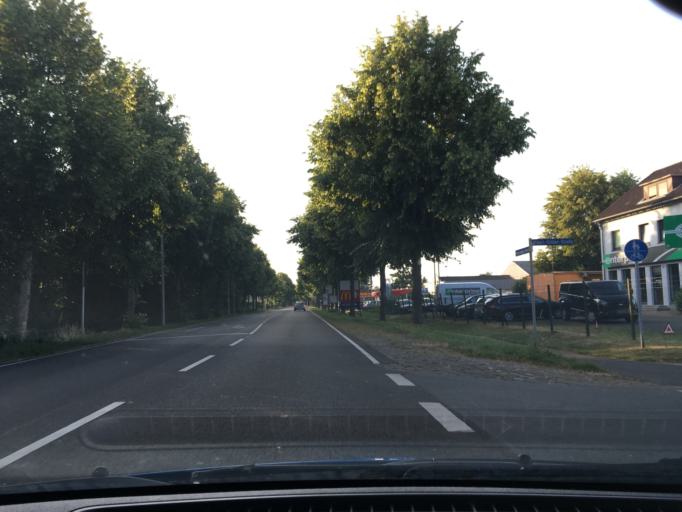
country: DE
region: Lower Saxony
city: Celle
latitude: 52.6095
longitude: 10.0999
